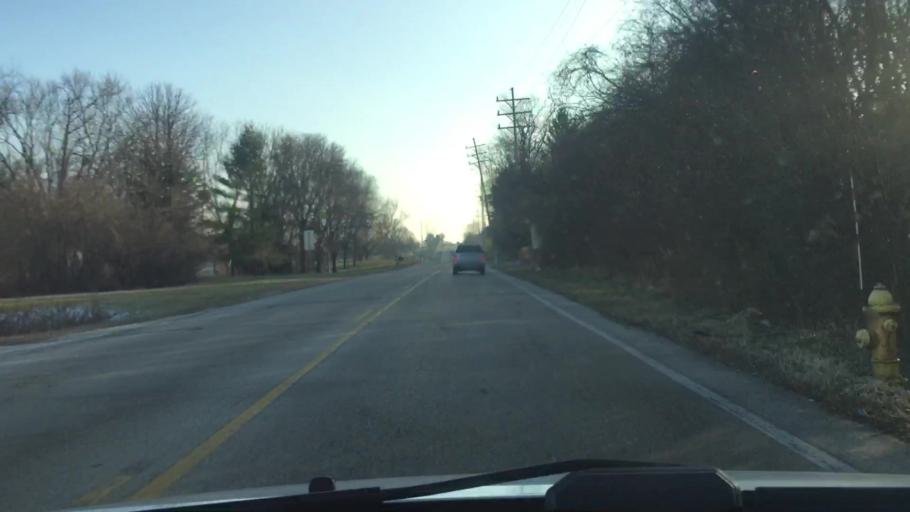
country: US
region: Wisconsin
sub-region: Waukesha County
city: Oconomowoc
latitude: 43.0956
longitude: -88.4958
